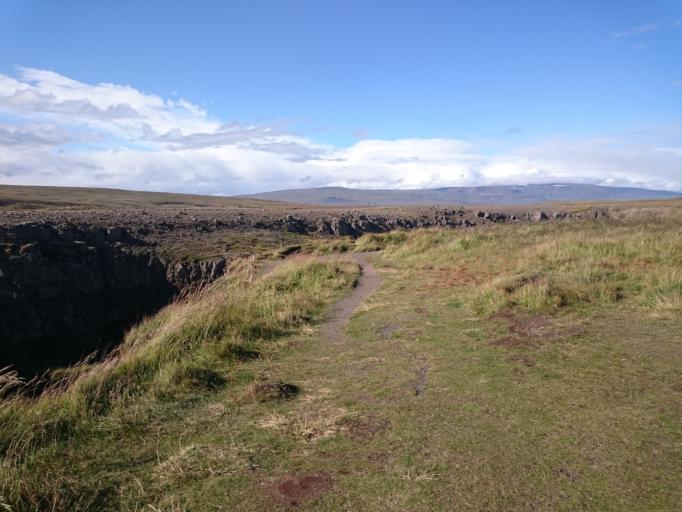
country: IS
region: Northwest
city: Saudarkrokur
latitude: 65.3327
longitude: -20.5702
